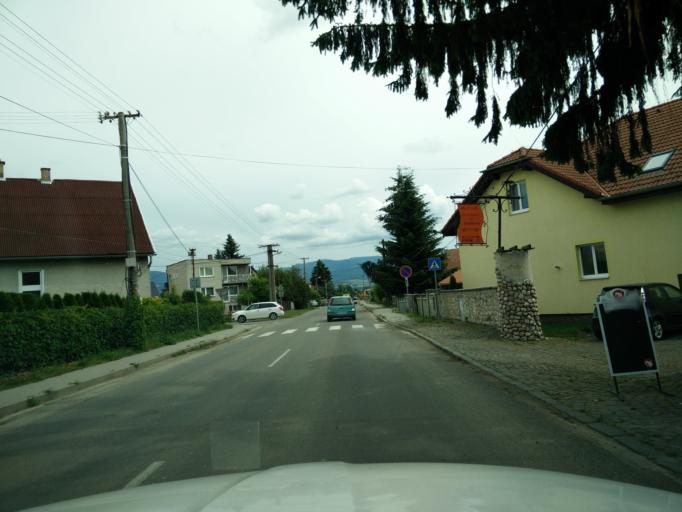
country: SK
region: Nitriansky
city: Bojnice
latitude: 48.7603
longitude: 18.5715
